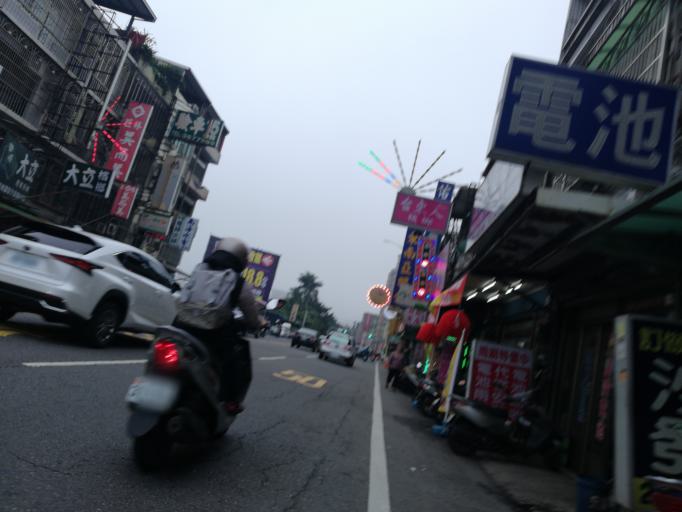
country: TW
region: Taiwan
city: Taoyuan City
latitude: 24.9778
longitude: 121.3035
